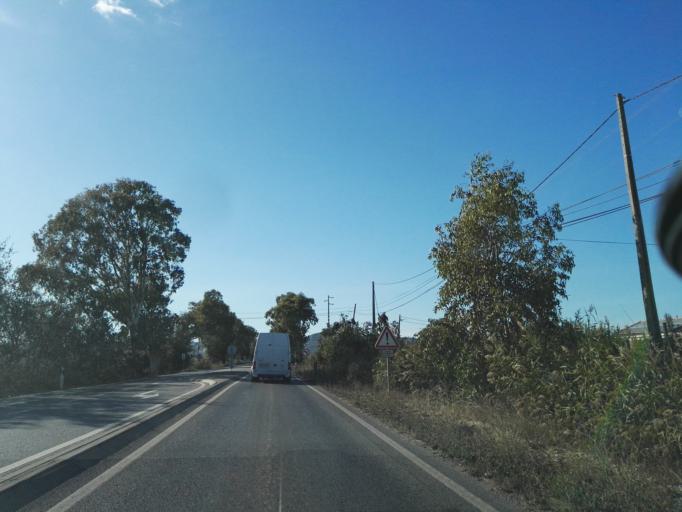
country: PT
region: Lisbon
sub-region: Vila Franca de Xira
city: Vila Franca de Xira
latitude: 38.9428
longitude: -8.9472
